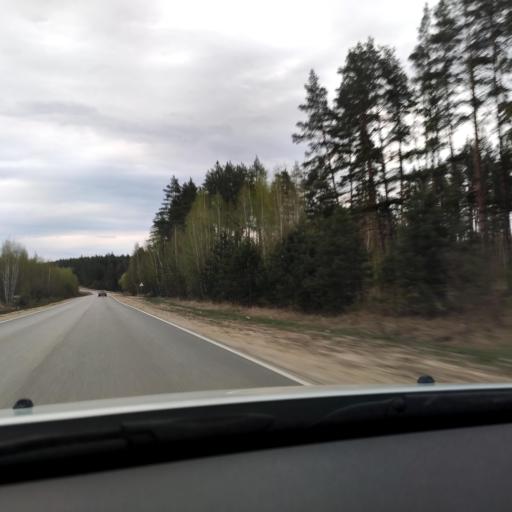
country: RU
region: Lipetsk
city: Zadonsk
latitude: 52.4223
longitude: 38.9467
